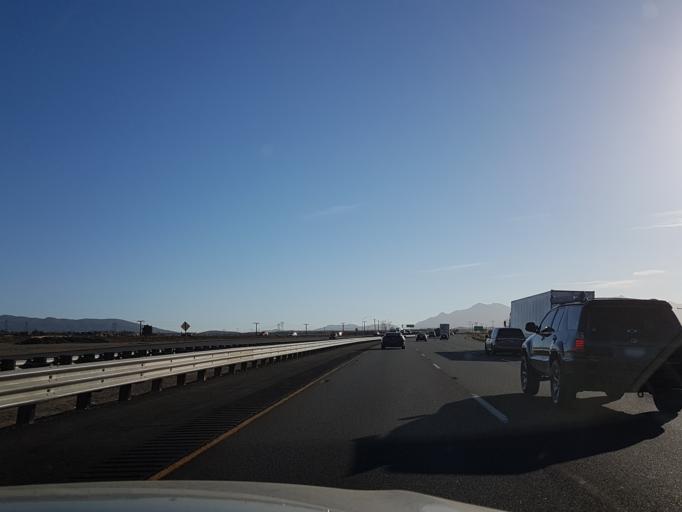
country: US
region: California
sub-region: San Bernardino County
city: Oak Hills
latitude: 34.3963
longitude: -117.4044
